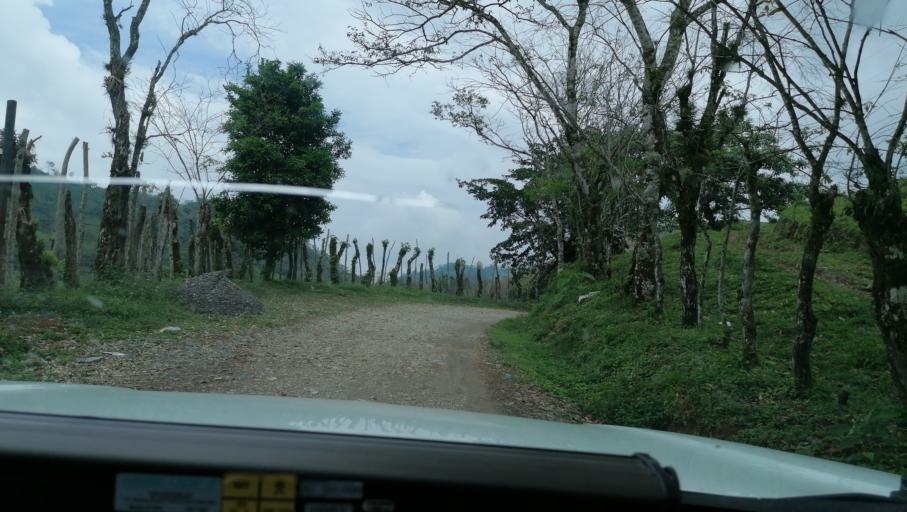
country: MX
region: Chiapas
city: Ocotepec
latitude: 17.3249
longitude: -93.1339
